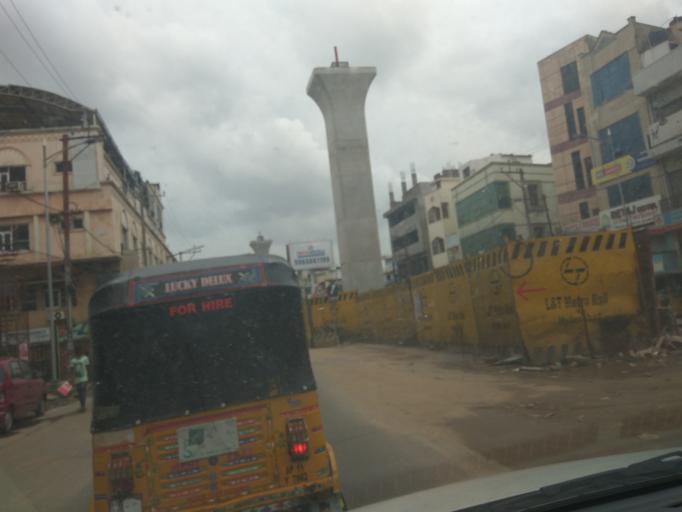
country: IN
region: Telangana
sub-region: Hyderabad
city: Malkajgiri
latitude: 17.4167
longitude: 78.4990
